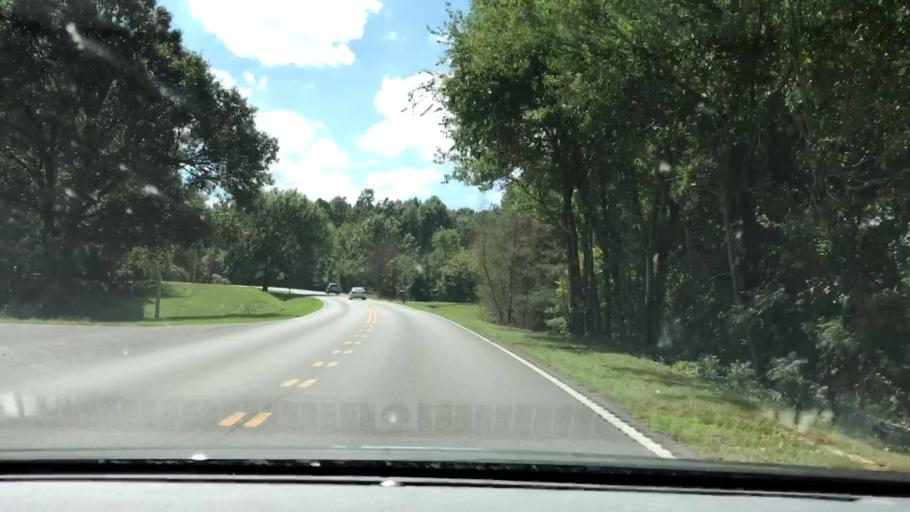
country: US
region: Kentucky
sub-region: McCracken County
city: Reidland
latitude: 36.9695
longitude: -88.5156
